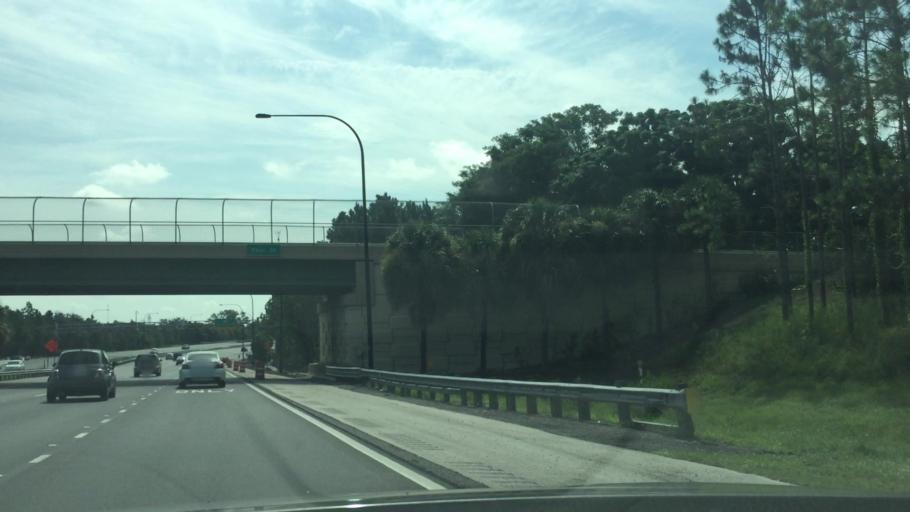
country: US
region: Florida
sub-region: Orange County
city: Orlovista
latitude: 28.5488
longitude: -81.4676
